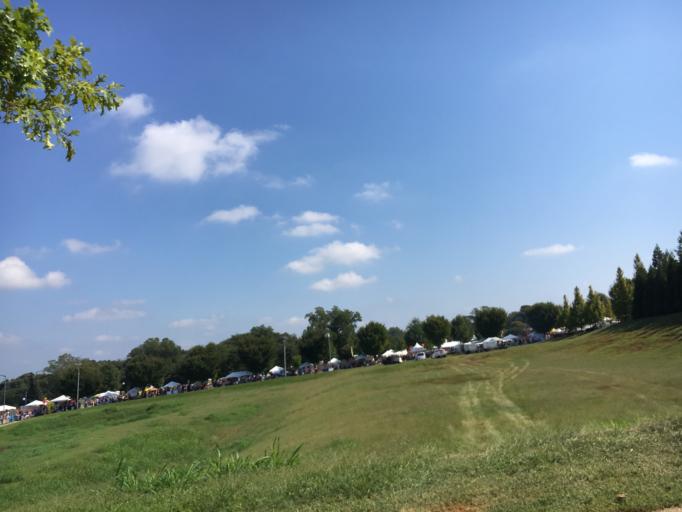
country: US
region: South Carolina
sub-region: Spartanburg County
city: Spartanburg
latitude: 34.9538
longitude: -81.9309
